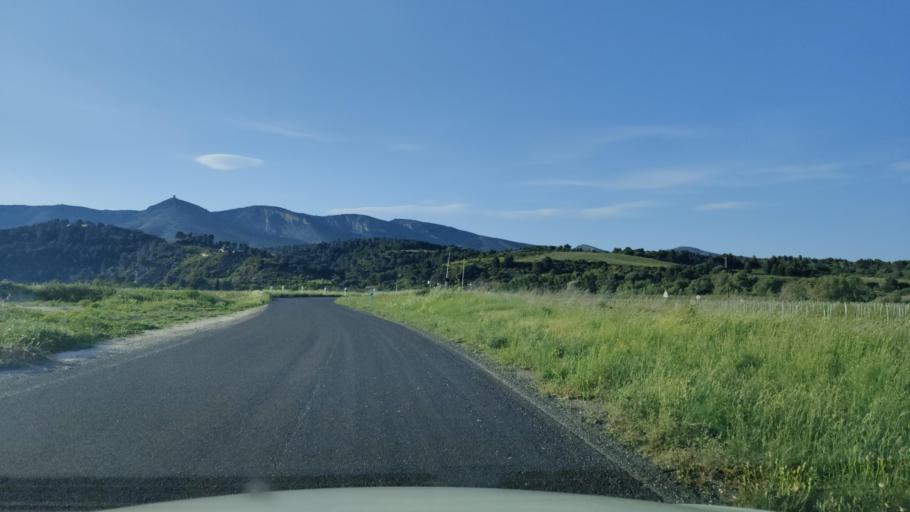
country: FR
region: Languedoc-Roussillon
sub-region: Departement des Pyrenees-Orientales
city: Baixas
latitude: 42.7789
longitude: 2.7776
